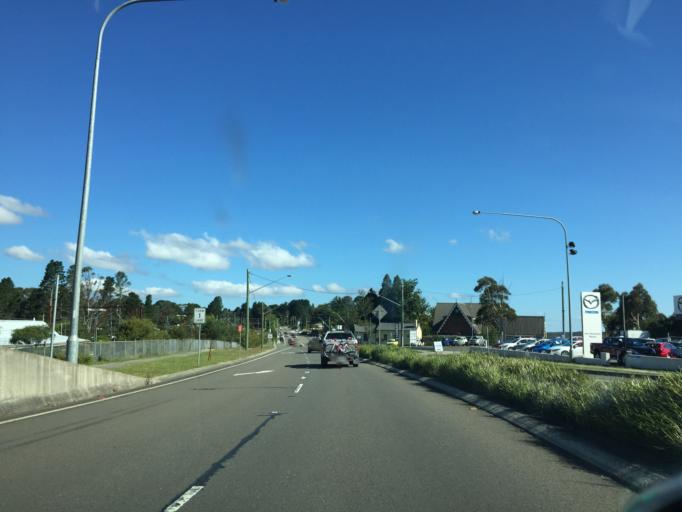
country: AU
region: New South Wales
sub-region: Blue Mountains Municipality
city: Blackheath
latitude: -33.6731
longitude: 150.2802
